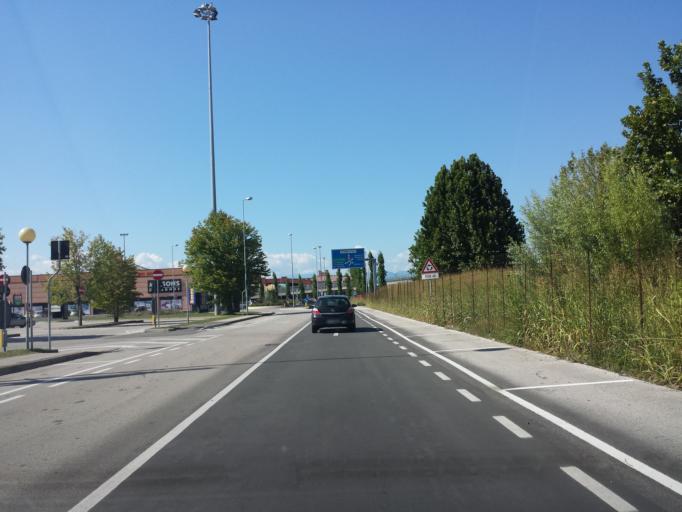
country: IT
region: Veneto
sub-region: Provincia di Vicenza
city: Torri di Quartesolo
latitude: 45.5109
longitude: 11.6267
